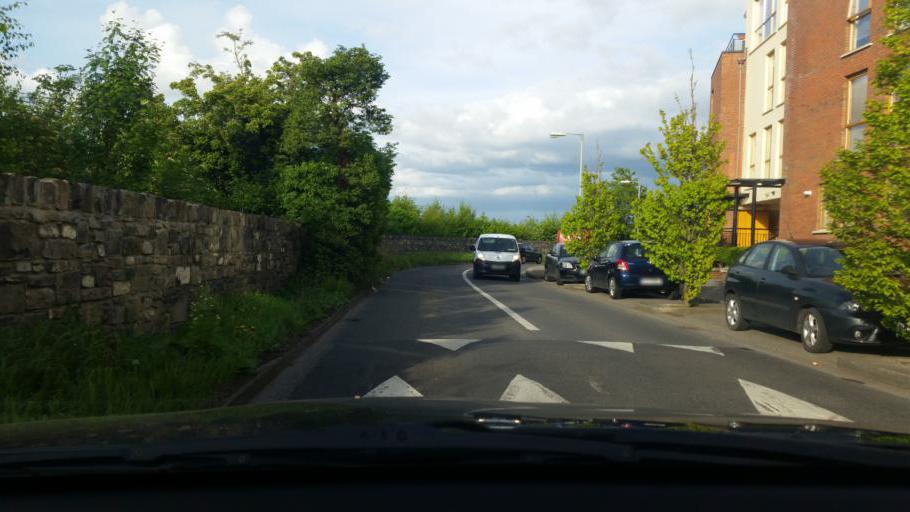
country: IE
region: Leinster
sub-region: Dublin City
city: Finglas
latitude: 53.3786
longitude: -6.3277
